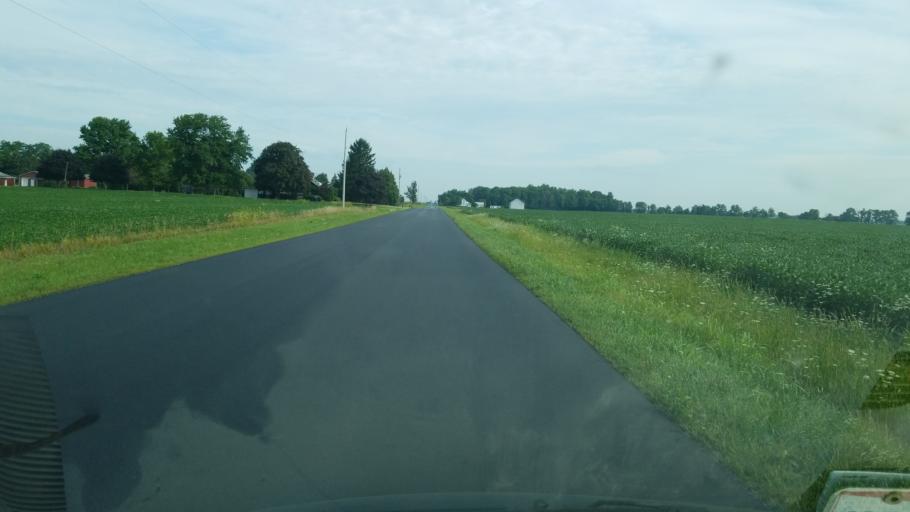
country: US
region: Ohio
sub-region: Crawford County
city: Bucyrus
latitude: 40.8518
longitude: -83.0166
